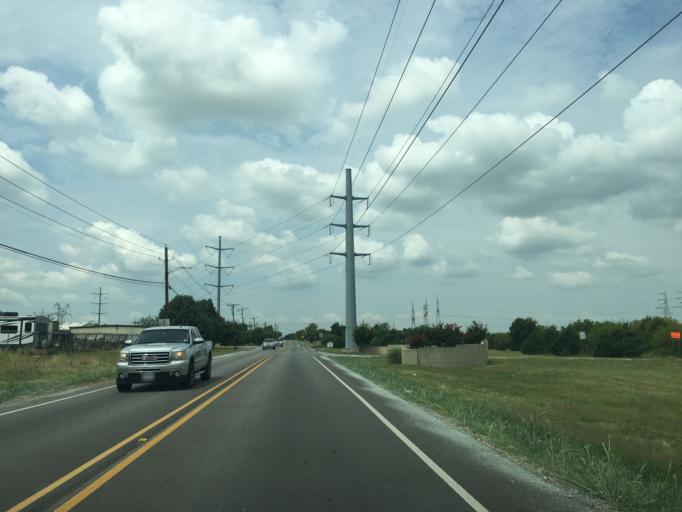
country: US
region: Texas
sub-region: Rockwall County
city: Royse City
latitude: 32.9727
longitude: -96.3429
